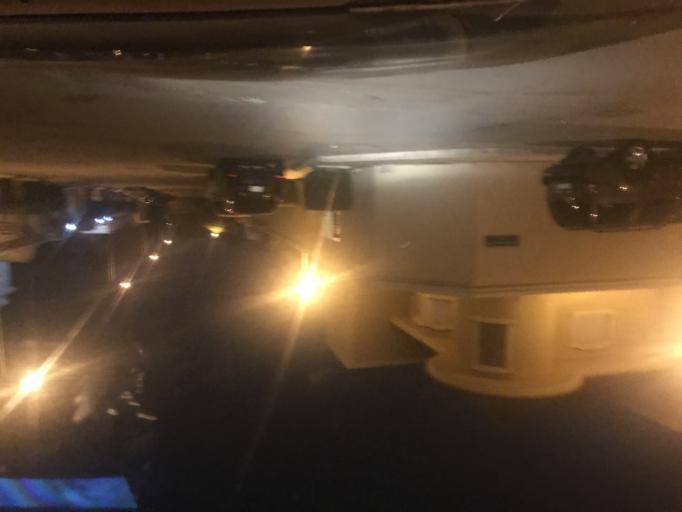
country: SA
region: Ar Riyad
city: Riyadh
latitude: 24.7498
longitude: 46.7507
